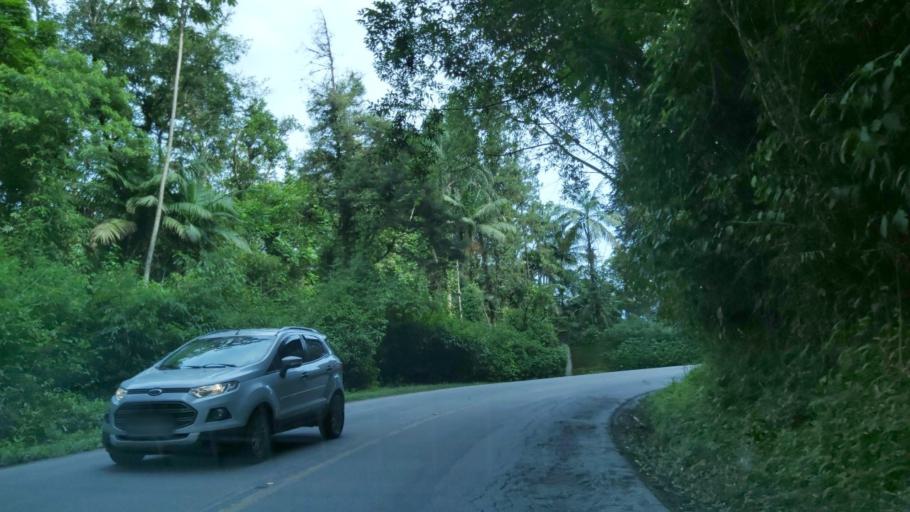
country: BR
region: Sao Paulo
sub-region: Miracatu
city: Miracatu
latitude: -24.0430
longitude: -47.5684
